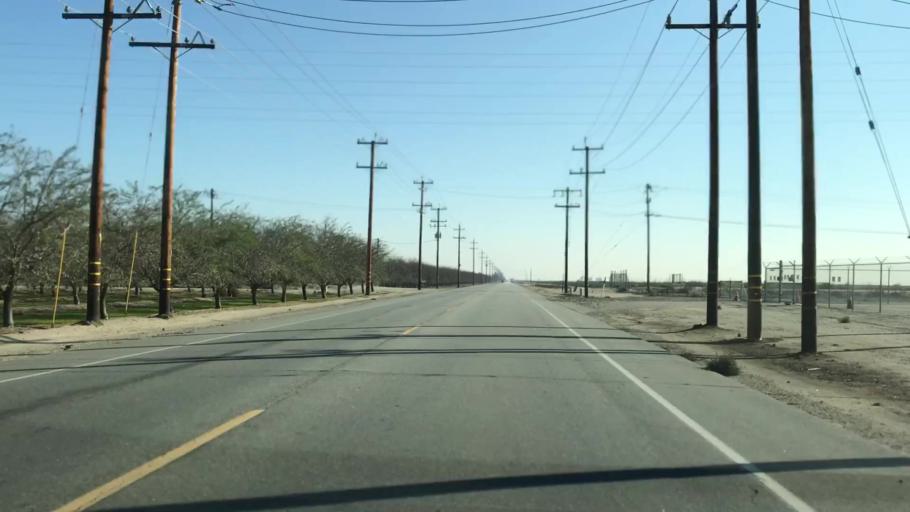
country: US
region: California
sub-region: Kern County
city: Rosedale
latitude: 35.3545
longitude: -119.2708
